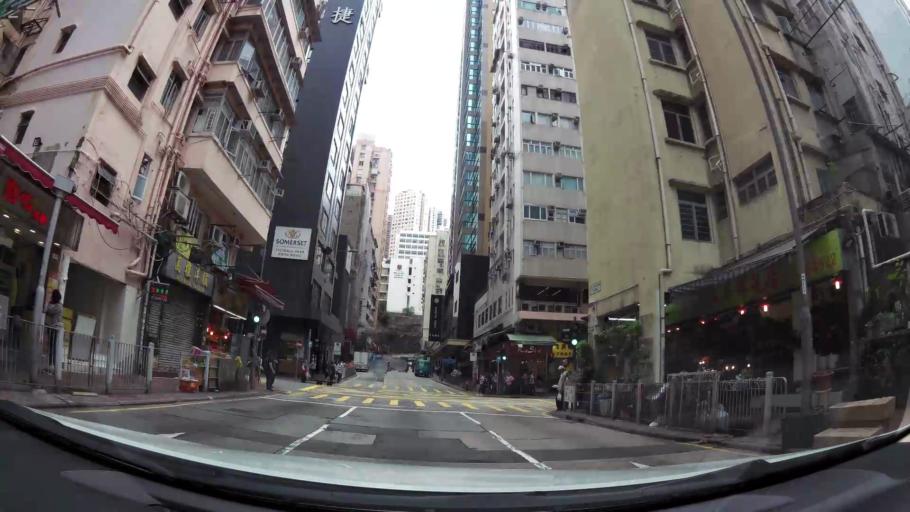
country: HK
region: Wanchai
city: Wan Chai
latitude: 22.2853
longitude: 114.1913
